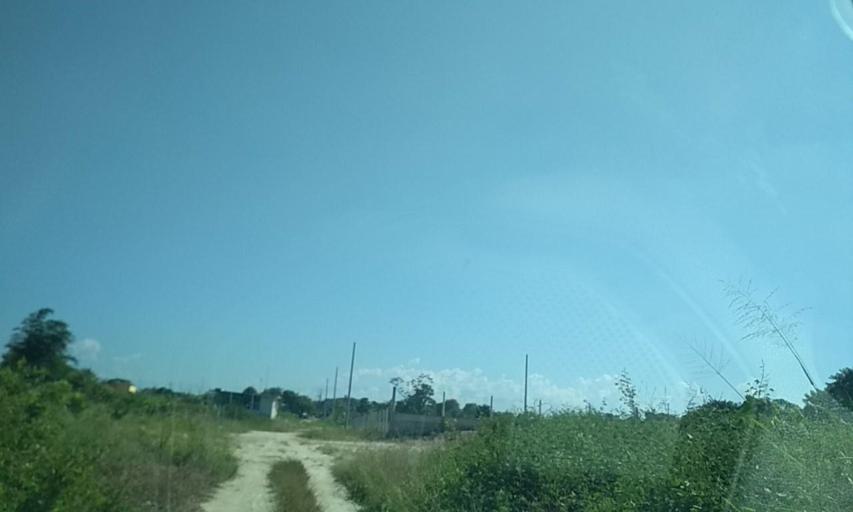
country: MX
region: Veracruz
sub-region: Martinez de la Torre
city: La Union Paso Largo
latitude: 20.1450
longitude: -97.0017
